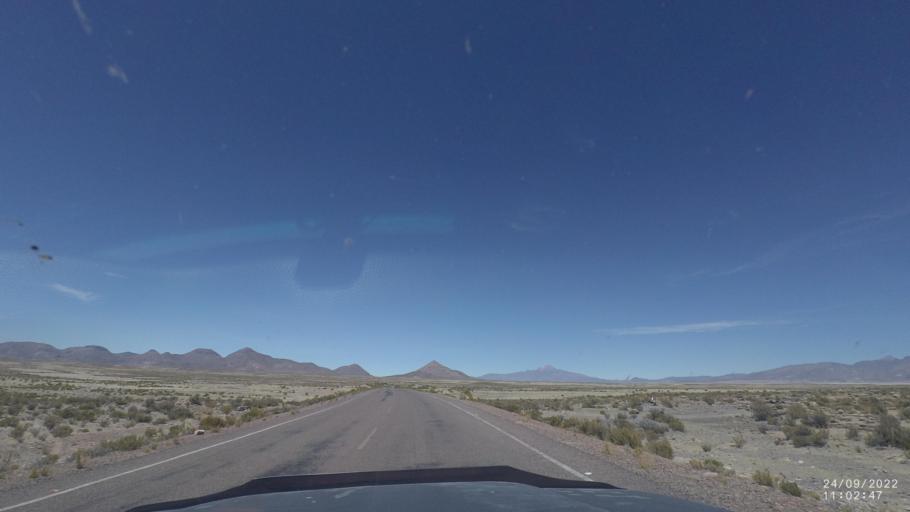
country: BO
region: Oruro
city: Challapata
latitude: -19.4692
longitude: -67.4279
